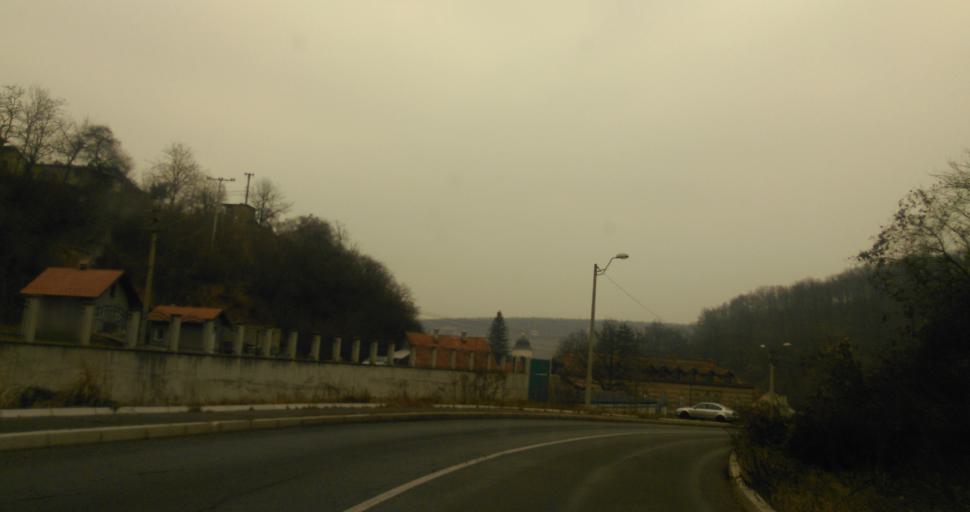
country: RS
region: Central Serbia
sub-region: Belgrade
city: Rakovica
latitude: 44.7291
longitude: 20.4466
